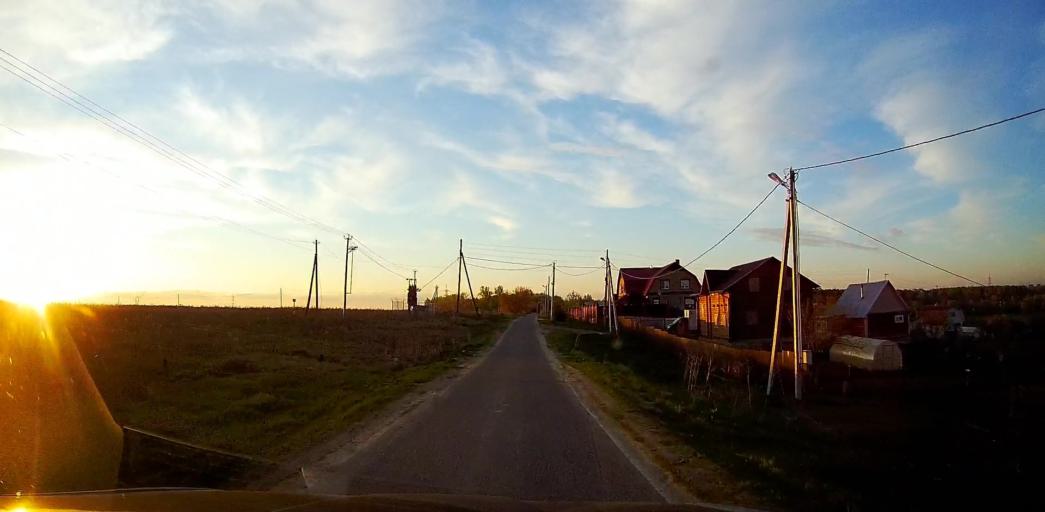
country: RU
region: Moskovskaya
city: Peski
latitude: 55.2276
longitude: 38.7342
